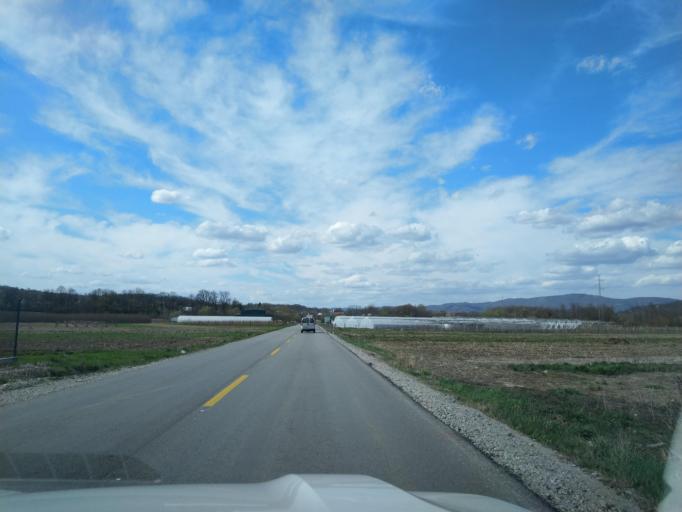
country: RS
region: Central Serbia
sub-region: Zlatiborski Okrug
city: Arilje
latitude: 43.7887
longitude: 20.1058
